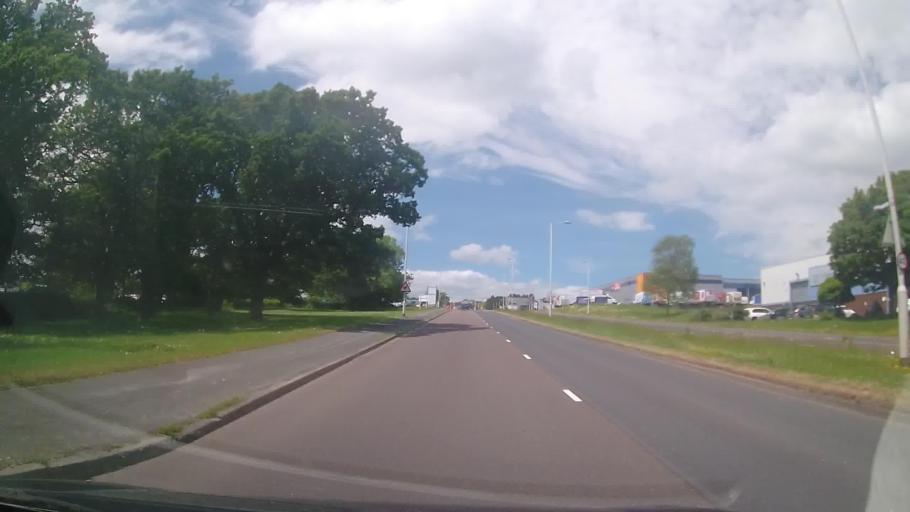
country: GB
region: England
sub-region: Devon
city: Plympton
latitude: 50.4174
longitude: -4.0913
